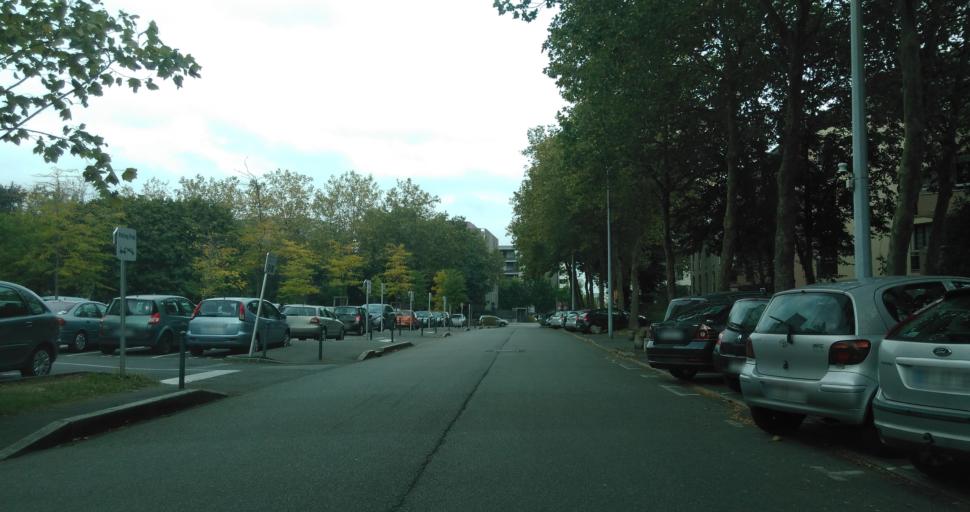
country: FR
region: Brittany
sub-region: Departement d'Ille-et-Vilaine
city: Rennes
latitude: 48.0910
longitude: -1.6764
